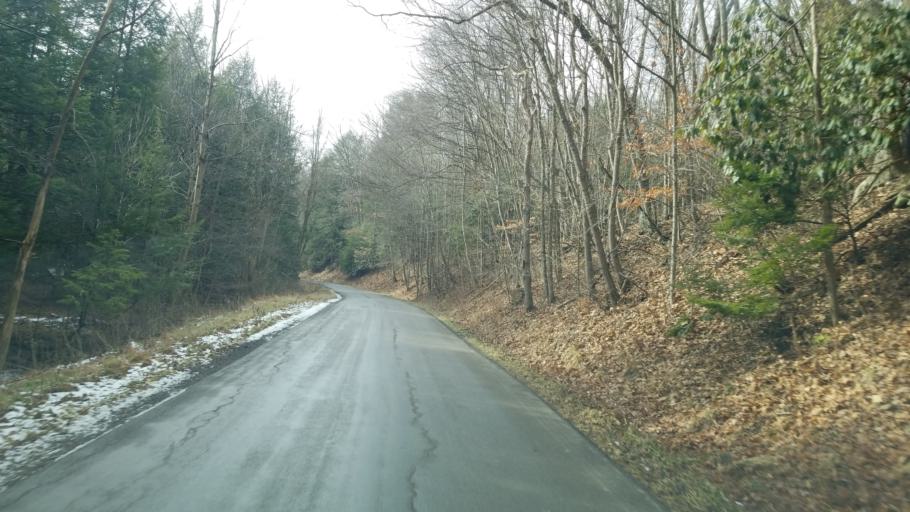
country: US
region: Pennsylvania
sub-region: Indiana County
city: Johnsonburg
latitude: 40.8280
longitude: -78.9670
